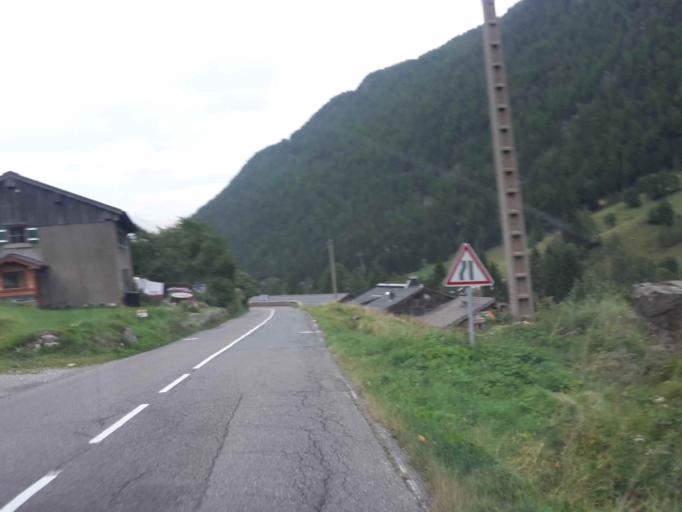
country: FR
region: Rhone-Alpes
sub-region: Departement de la Haute-Savoie
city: Chamonix-Mont-Blanc
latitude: 46.0289
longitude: 6.9271
